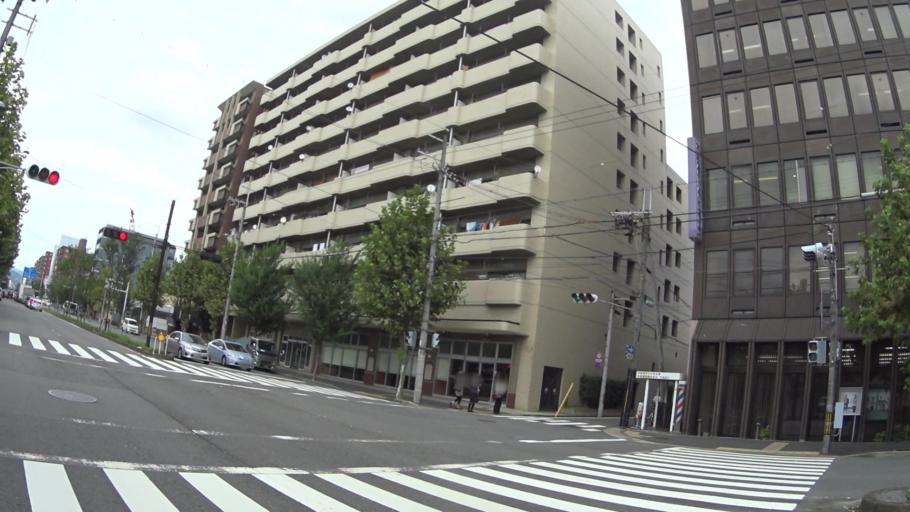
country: JP
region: Kyoto
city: Kyoto
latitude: 34.9943
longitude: 135.7327
